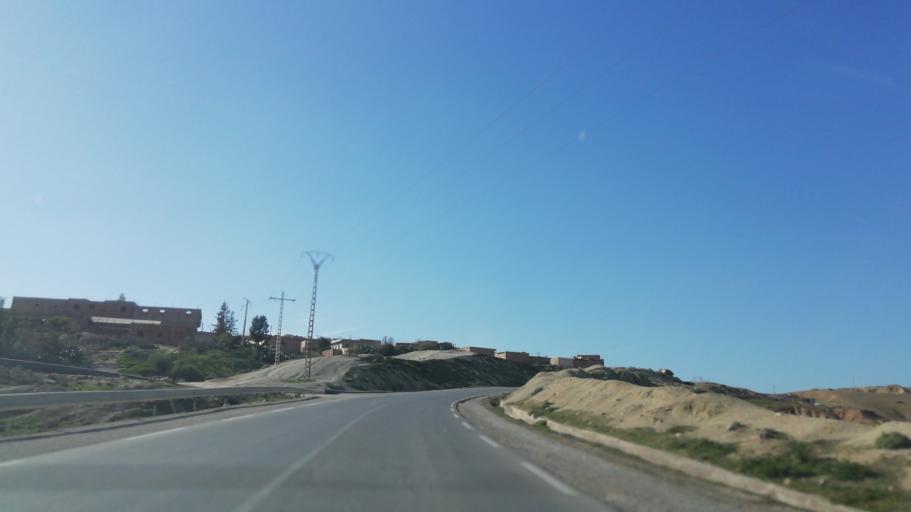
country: DZ
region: Mascara
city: Oued el Abtal
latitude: 35.4551
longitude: 0.7122
